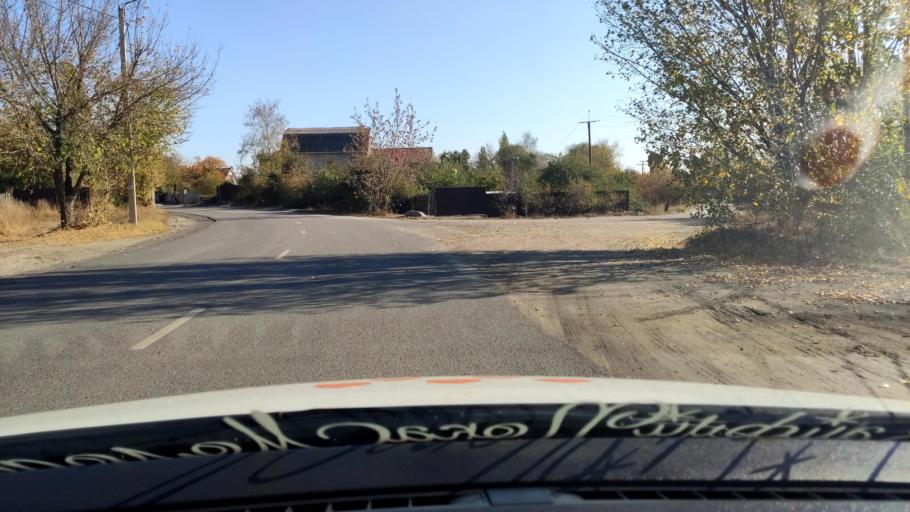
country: RU
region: Voronezj
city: Pridonskoy
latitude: 51.6838
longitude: 39.0669
